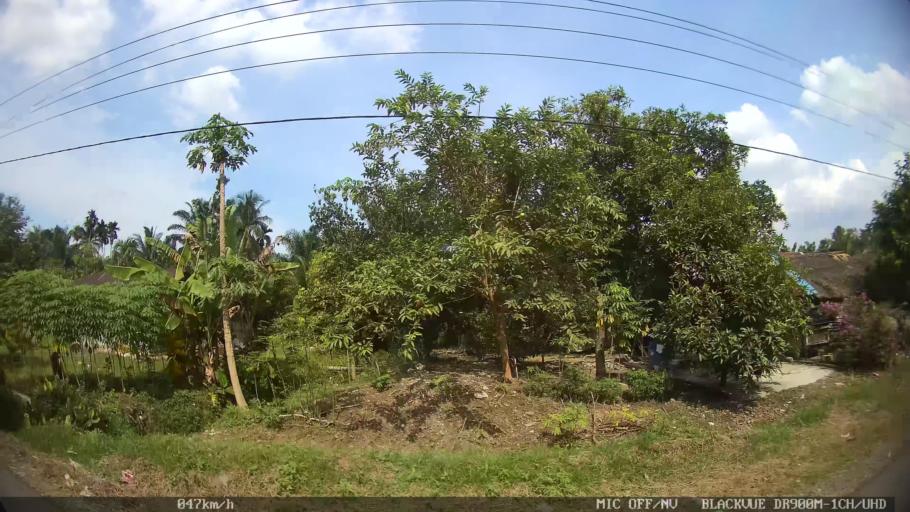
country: ID
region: North Sumatra
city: Binjai
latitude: 3.6452
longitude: 98.5177
